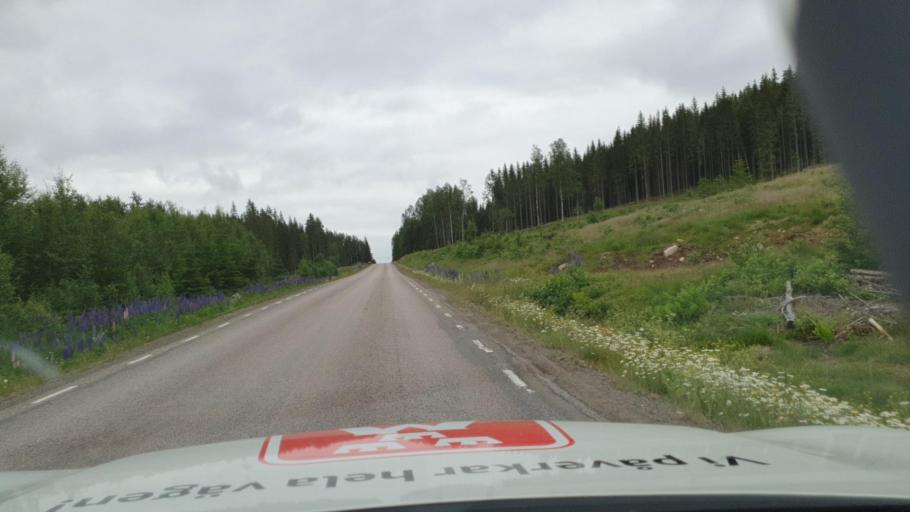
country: SE
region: Vaermland
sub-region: Torsby Kommun
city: Torsby
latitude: 59.9276
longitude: 12.8506
